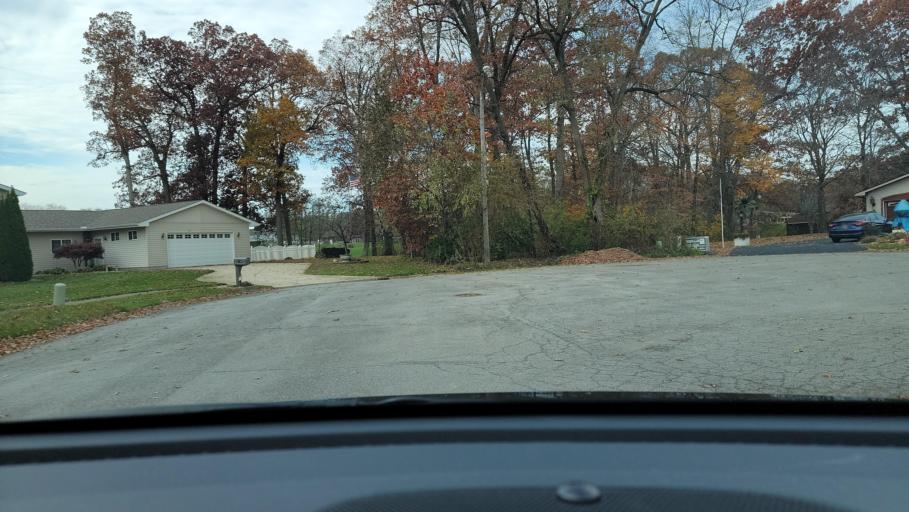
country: US
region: Indiana
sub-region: Porter County
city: Portage
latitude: 41.5831
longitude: -87.1484
